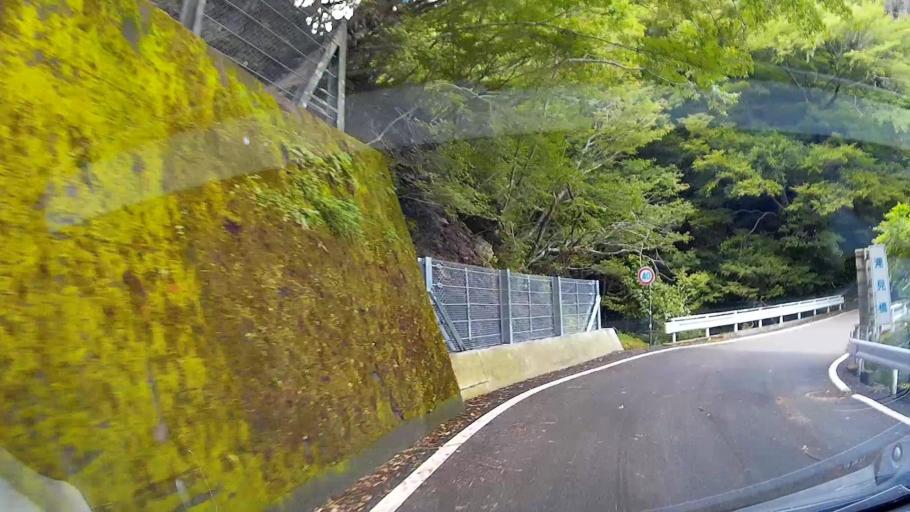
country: JP
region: Shizuoka
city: Shizuoka-shi
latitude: 35.2462
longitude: 138.2427
